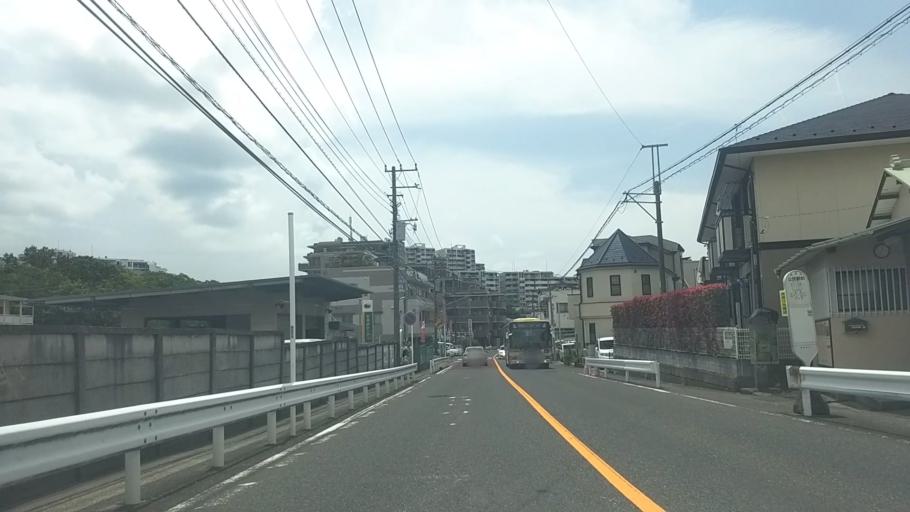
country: JP
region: Kanagawa
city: Fujisawa
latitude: 35.3470
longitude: 139.4927
